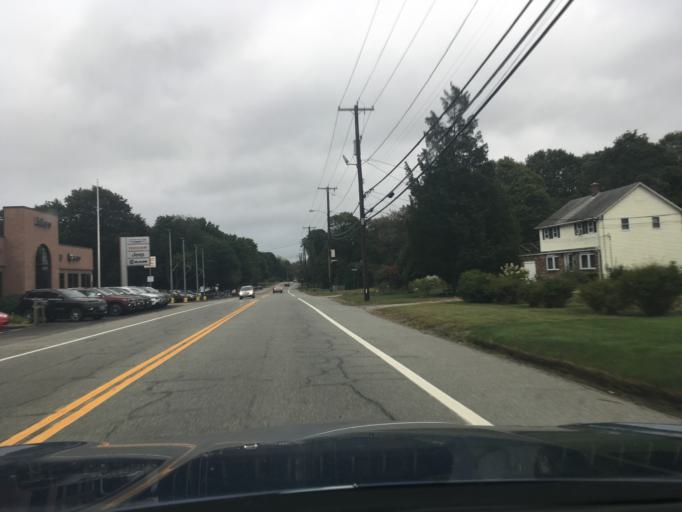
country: US
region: Rhode Island
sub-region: Washington County
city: North Kingstown
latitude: 41.5711
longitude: -71.4788
